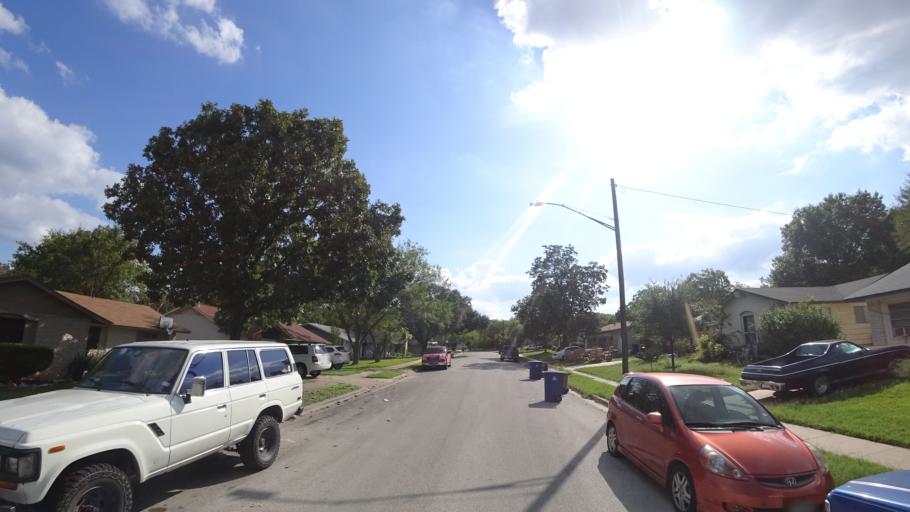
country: US
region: Texas
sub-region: Travis County
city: Wells Branch
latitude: 30.3585
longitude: -97.7095
